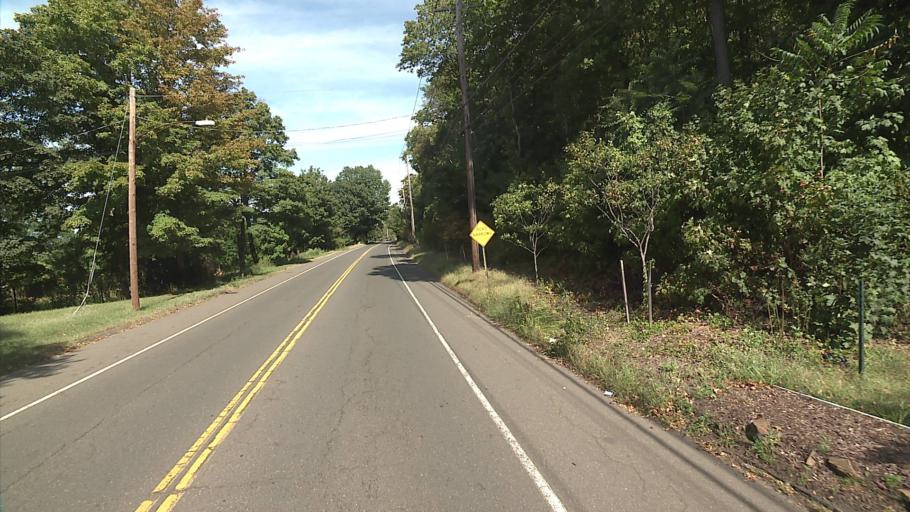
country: US
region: Connecticut
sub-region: New Haven County
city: North Haven
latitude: 41.3345
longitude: -72.8671
